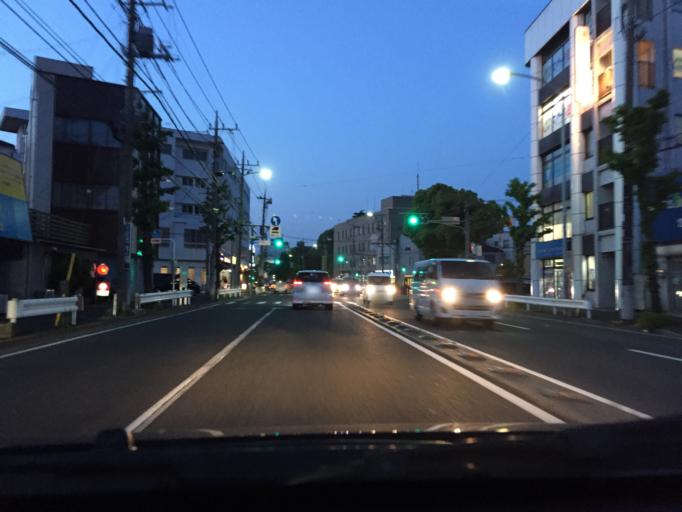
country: JP
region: Kanagawa
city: Yokohama
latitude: 35.4212
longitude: 139.6012
